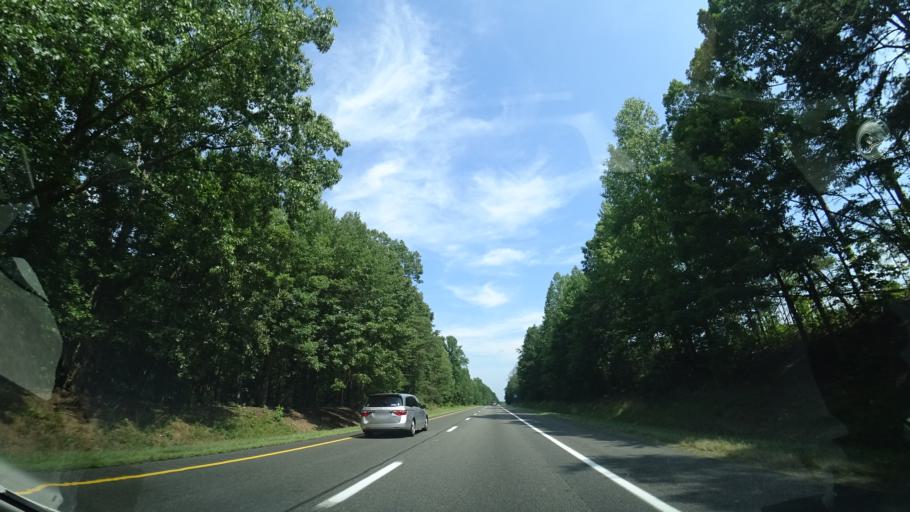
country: US
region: Virginia
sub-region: Louisa County
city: Louisa
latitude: 37.8630
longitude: -78.0041
